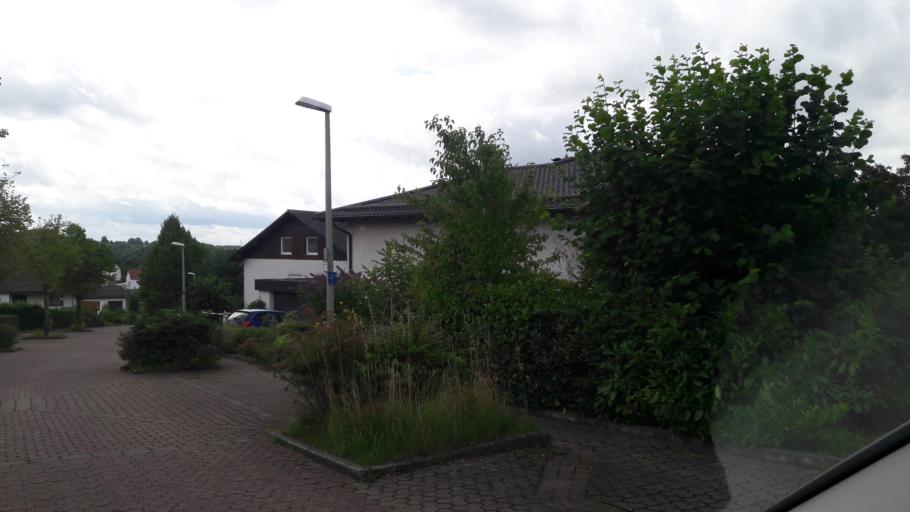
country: DE
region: Saarland
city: Tholey
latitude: 49.4979
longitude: 6.9802
